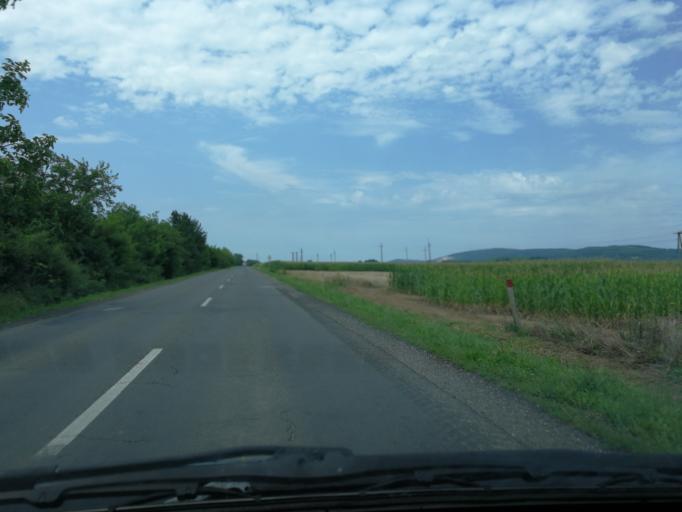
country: HU
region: Baranya
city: Siklos
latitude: 45.8496
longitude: 18.3536
